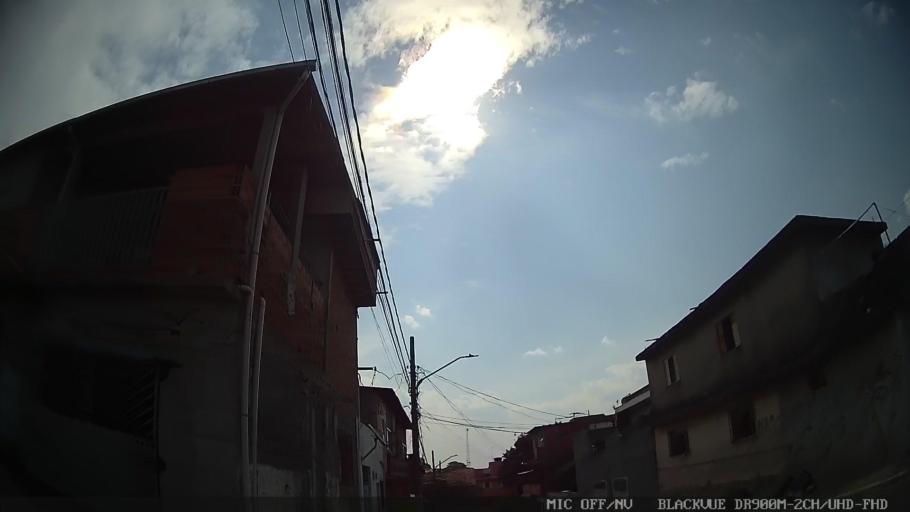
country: BR
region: Sao Paulo
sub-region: Ferraz De Vasconcelos
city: Ferraz de Vasconcelos
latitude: -23.5010
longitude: -46.4152
